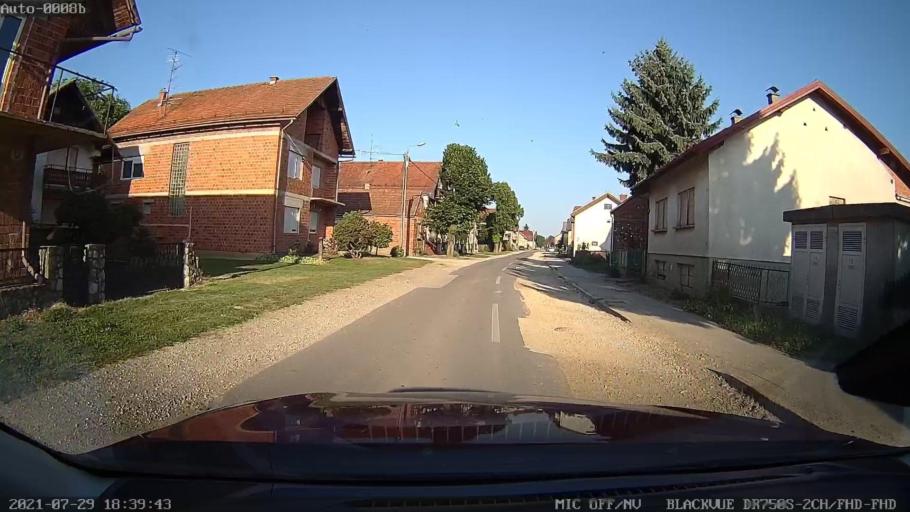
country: HR
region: Varazdinska
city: Petrijanec
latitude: 46.3212
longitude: 16.2241
